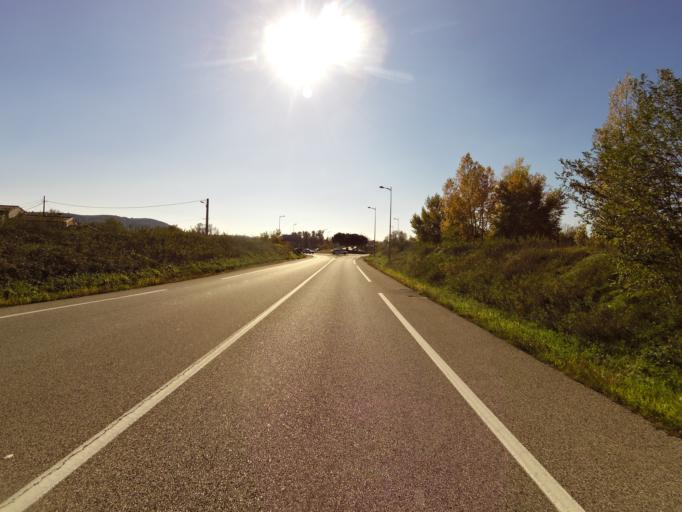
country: FR
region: Rhone-Alpes
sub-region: Departement de l'Ardeche
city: Saint-Privat
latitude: 44.6267
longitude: 4.4194
